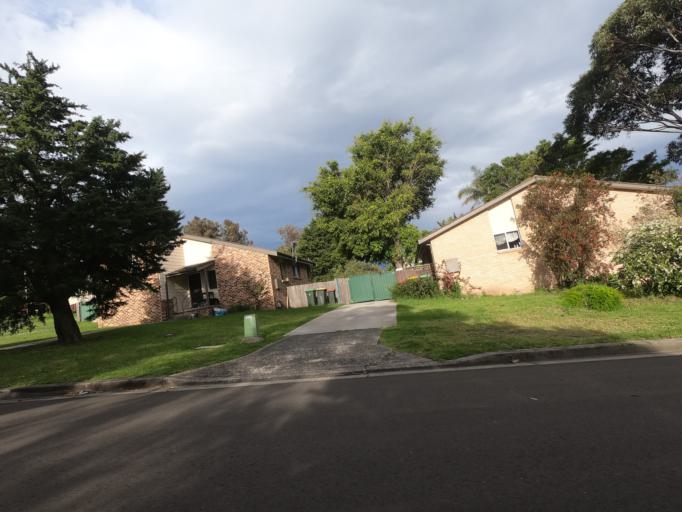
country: AU
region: New South Wales
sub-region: Wollongong
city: Berkeley
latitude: -34.4763
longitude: 150.8505
